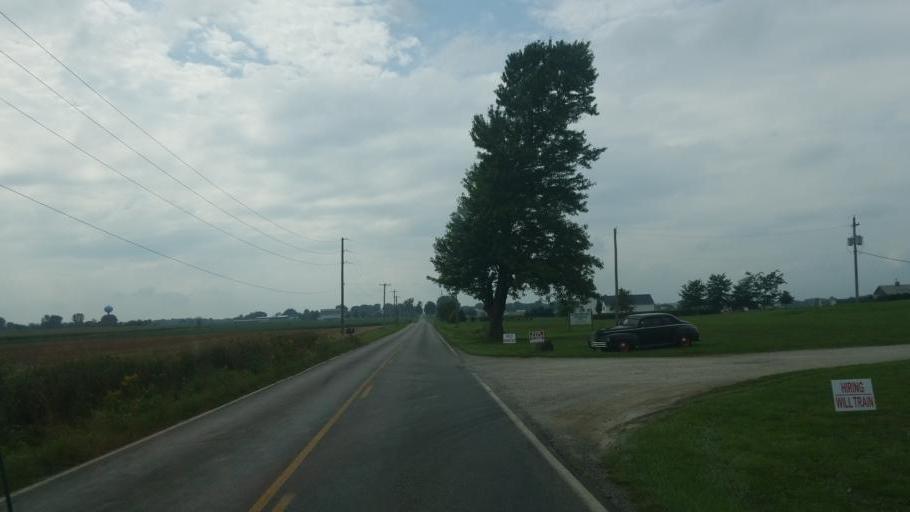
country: US
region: Ohio
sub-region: Wayne County
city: Creston
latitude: 40.9603
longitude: -81.8818
